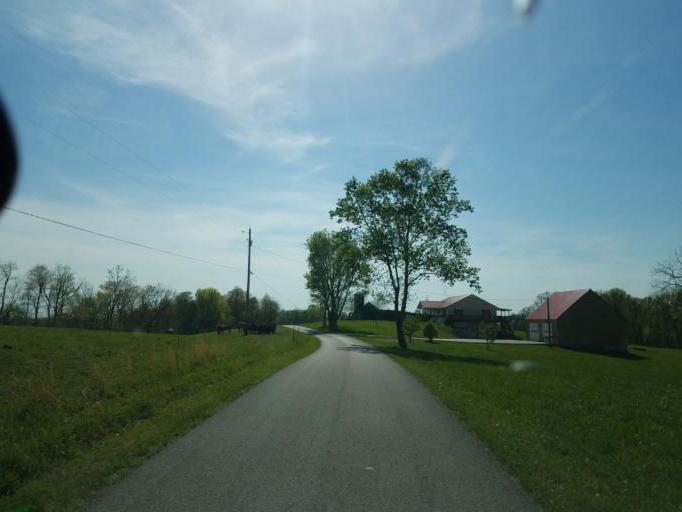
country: US
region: Kentucky
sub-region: Barren County
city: Cave City
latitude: 37.1225
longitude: -86.1013
